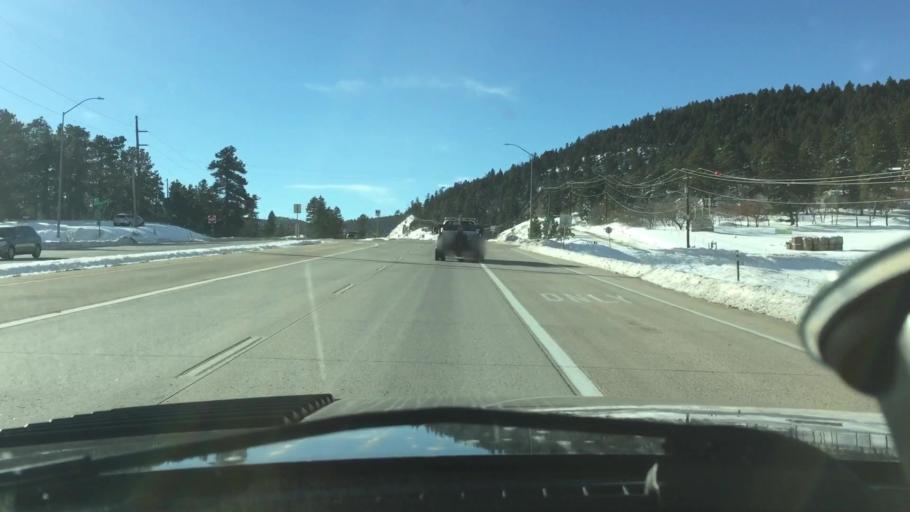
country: US
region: Colorado
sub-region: Jefferson County
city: Indian Hills
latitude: 39.5644
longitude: -105.2391
